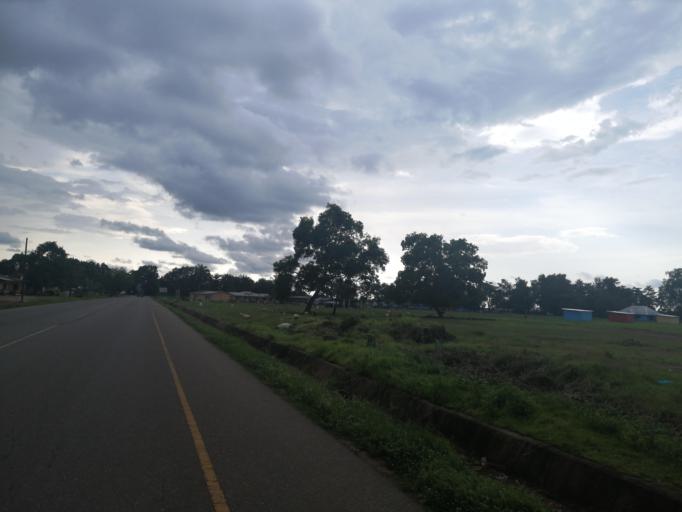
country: SL
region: Northern Province
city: Port Loko
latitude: 8.7749
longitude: -12.7904
